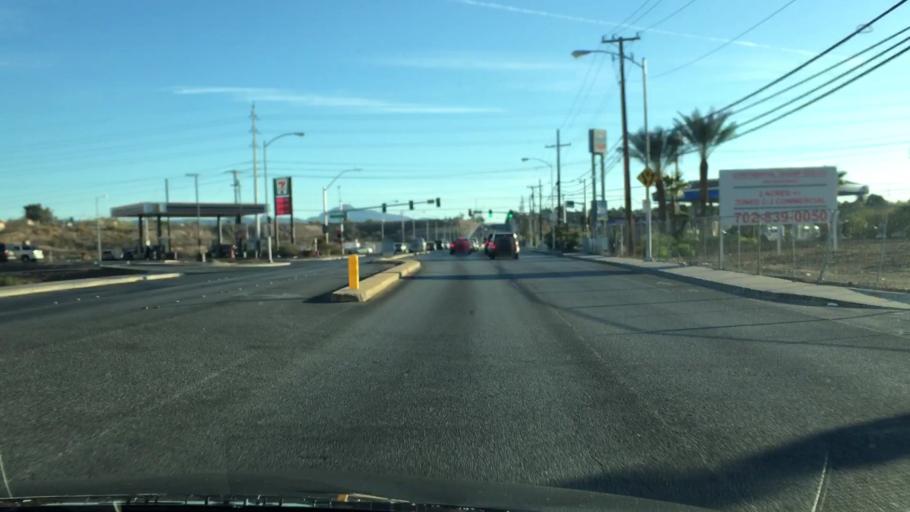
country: US
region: Nevada
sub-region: Clark County
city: Whitney
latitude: 36.0868
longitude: -115.0732
